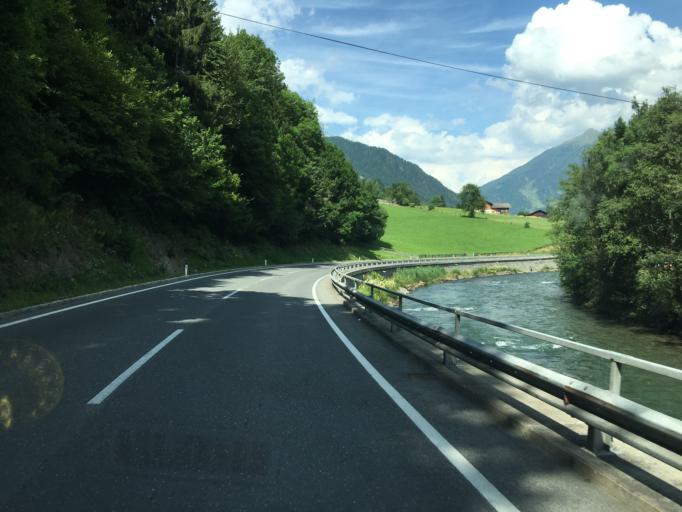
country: AT
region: Carinthia
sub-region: Politischer Bezirk Spittal an der Drau
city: Rangersdorf
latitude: 46.8786
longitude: 13.0044
